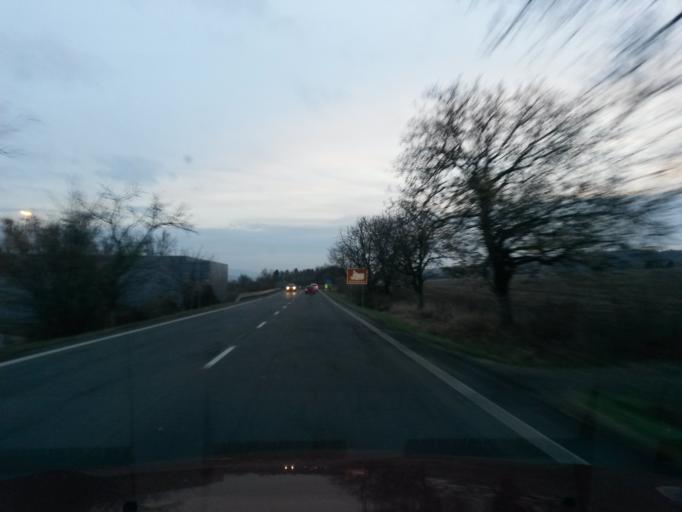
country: SK
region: Kosicky
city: Kosice
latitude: 48.7921
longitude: 21.3067
